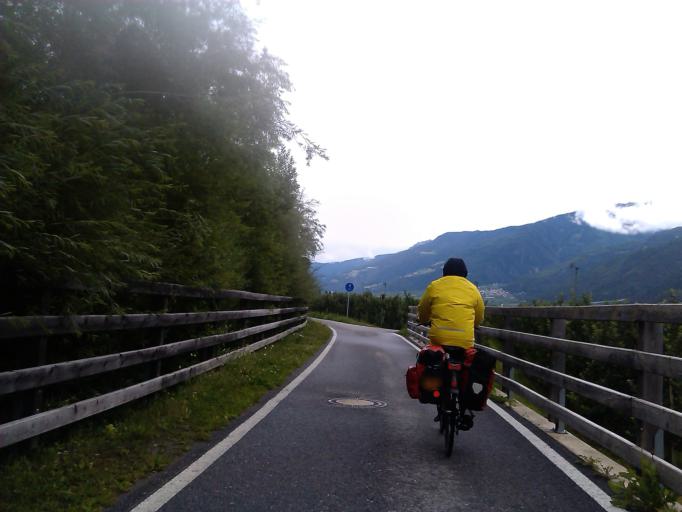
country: IT
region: Trentino-Alto Adige
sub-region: Bolzano
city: Silandro
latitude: 46.6166
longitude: 10.7911
